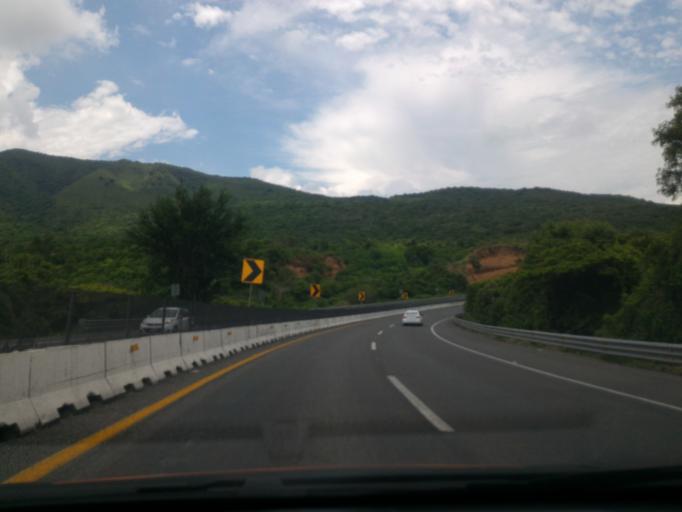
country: MX
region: Jalisco
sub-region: Acatlan de Juarez
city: Villa de los Ninos
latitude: 20.3956
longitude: -103.5542
